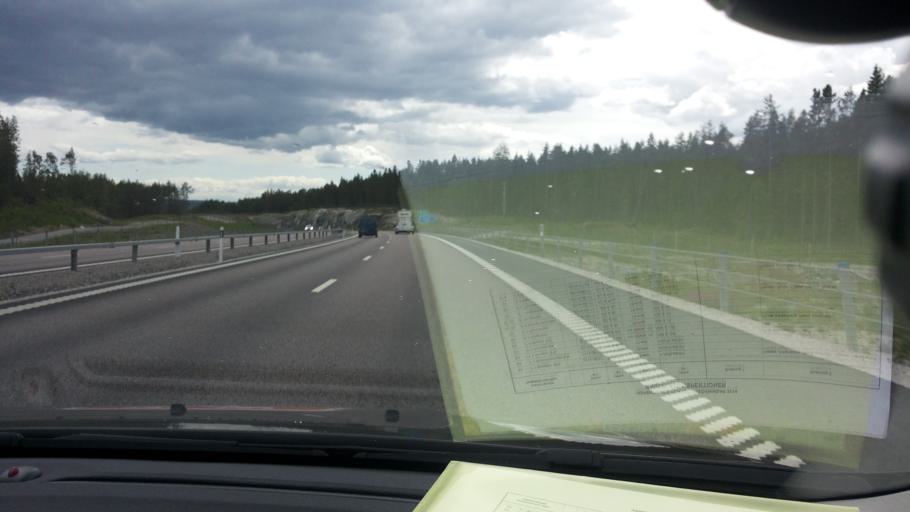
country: SE
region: Vaesternorrland
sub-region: Sundsvalls Kommun
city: Nolby
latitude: 62.3087
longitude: 17.3421
